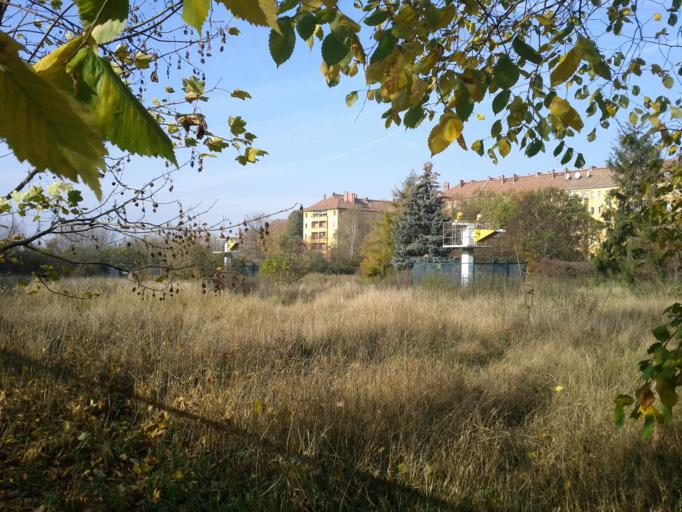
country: DE
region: Berlin
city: Tempelhof Bezirk
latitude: 52.4713
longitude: 13.4226
